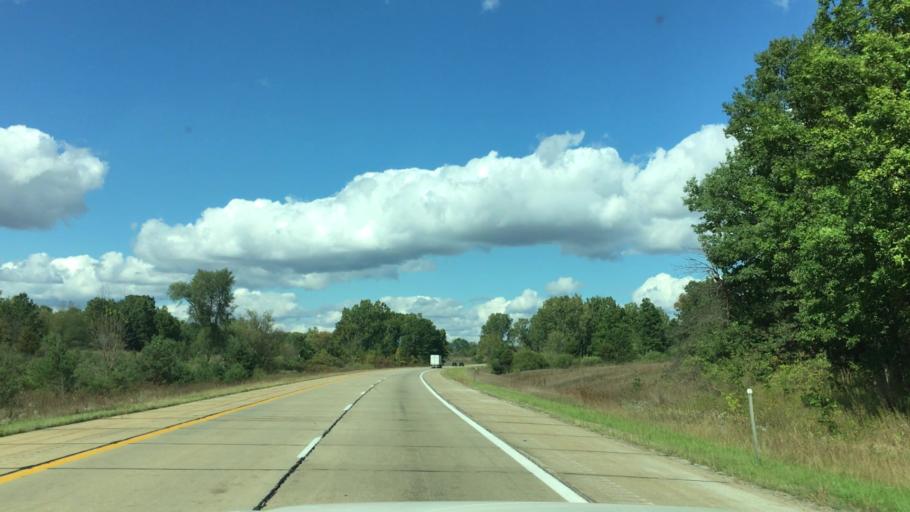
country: US
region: Michigan
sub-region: Eaton County
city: Olivet
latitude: 42.3987
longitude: -84.9684
